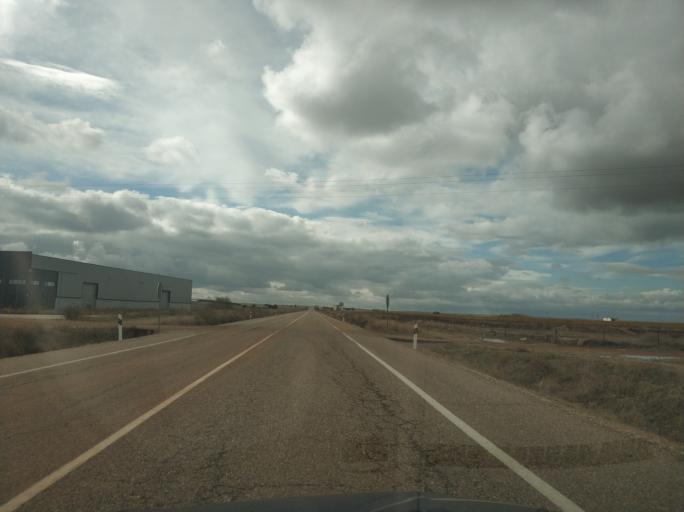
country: ES
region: Castille and Leon
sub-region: Provincia de Valladolid
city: Pollos
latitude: 41.4287
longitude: -5.1113
